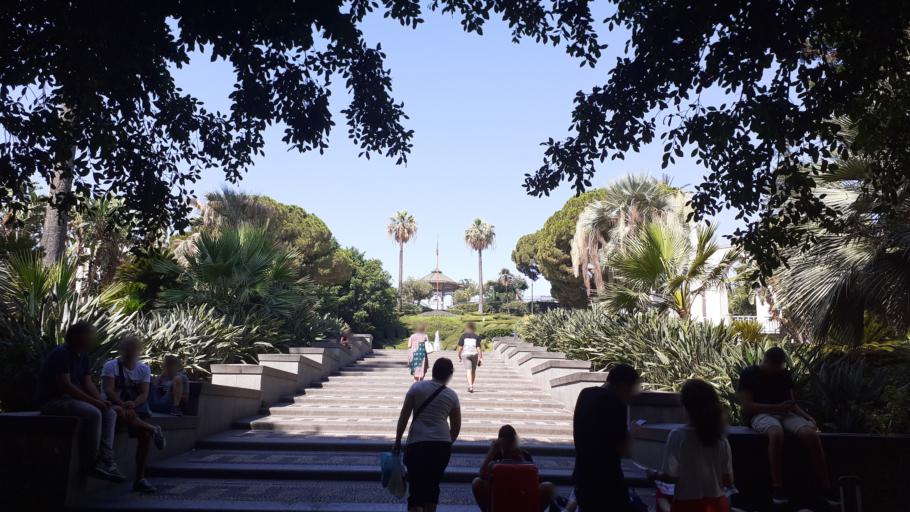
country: IT
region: Sicily
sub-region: Catania
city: Catania
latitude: 37.5108
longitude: 15.0853
